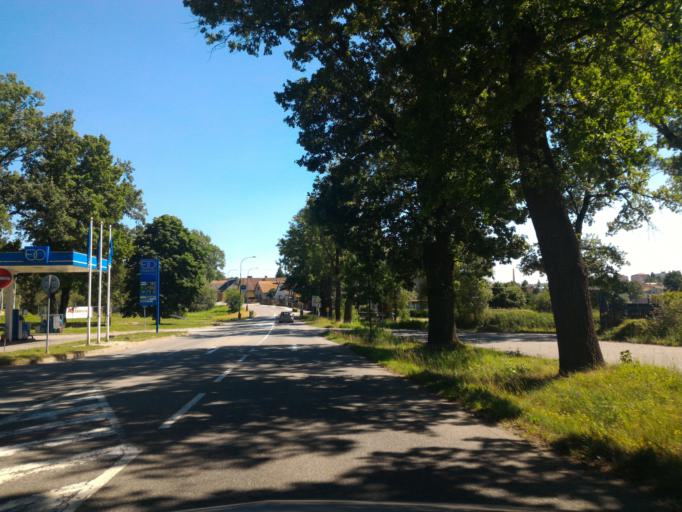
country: CZ
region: Vysocina
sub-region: Okres Jihlava
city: Trest'
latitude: 49.2988
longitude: 15.4829
